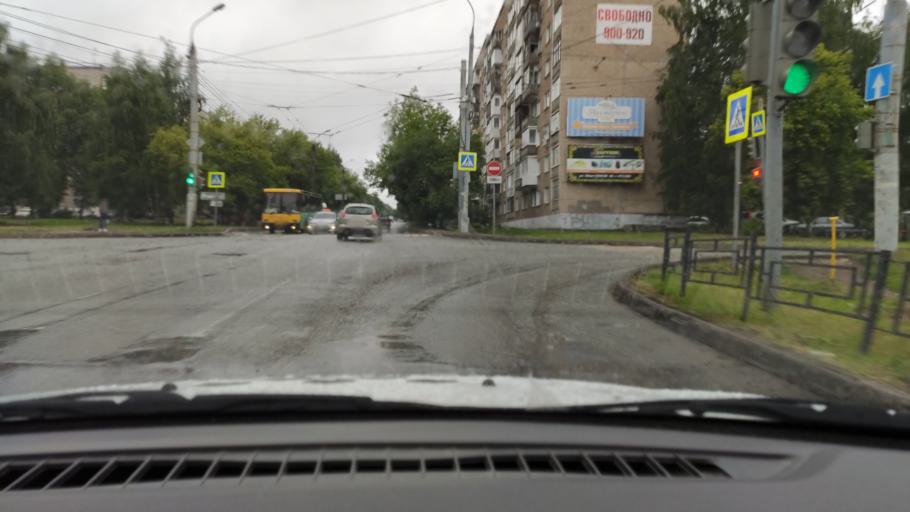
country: RU
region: Udmurtiya
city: Izhevsk
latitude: 56.8768
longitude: 53.1941
